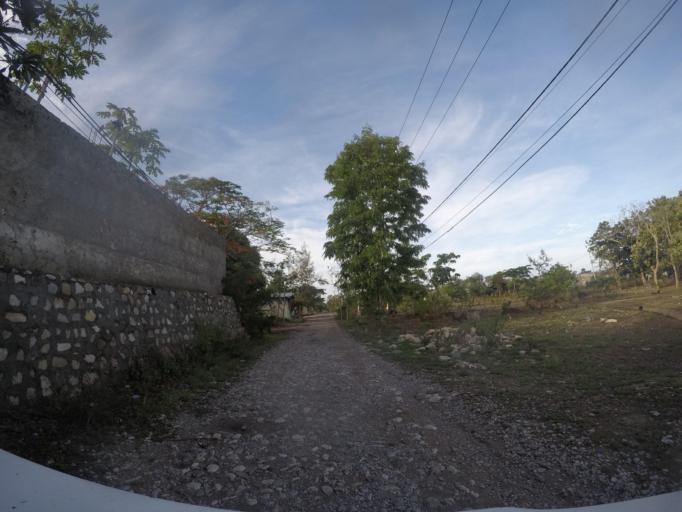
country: TL
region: Baucau
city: Baucau
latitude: -8.4879
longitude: 126.4523
